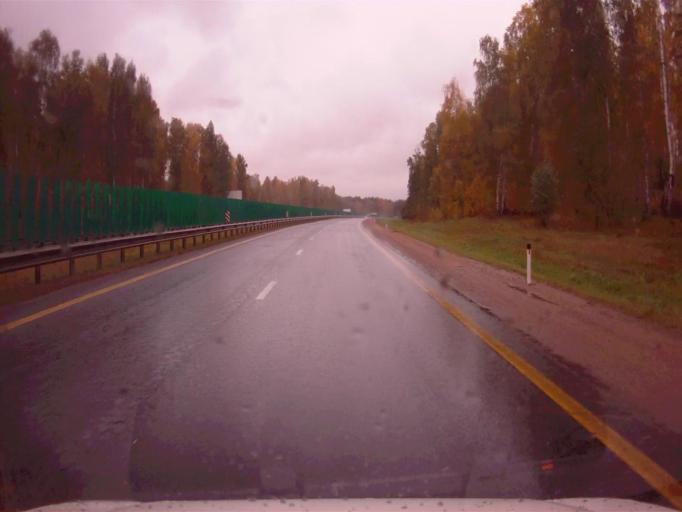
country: RU
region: Chelyabinsk
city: Dolgoderevenskoye
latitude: 55.3352
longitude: 61.3117
